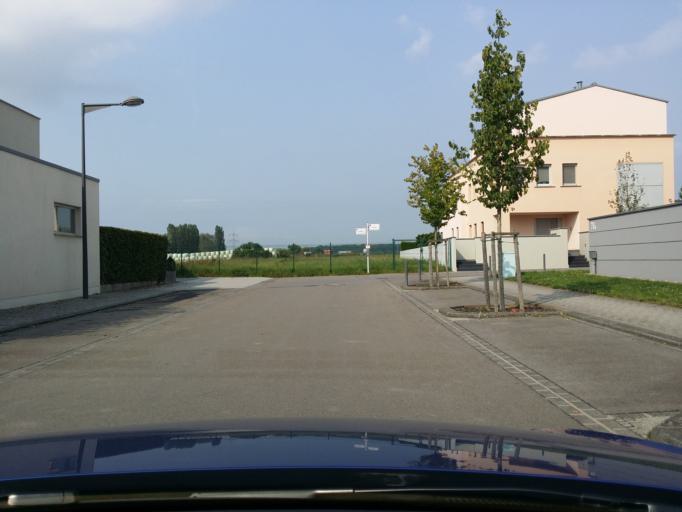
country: LU
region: Luxembourg
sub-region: Canton de Luxembourg
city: Bertrange
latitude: 49.6122
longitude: 6.0455
